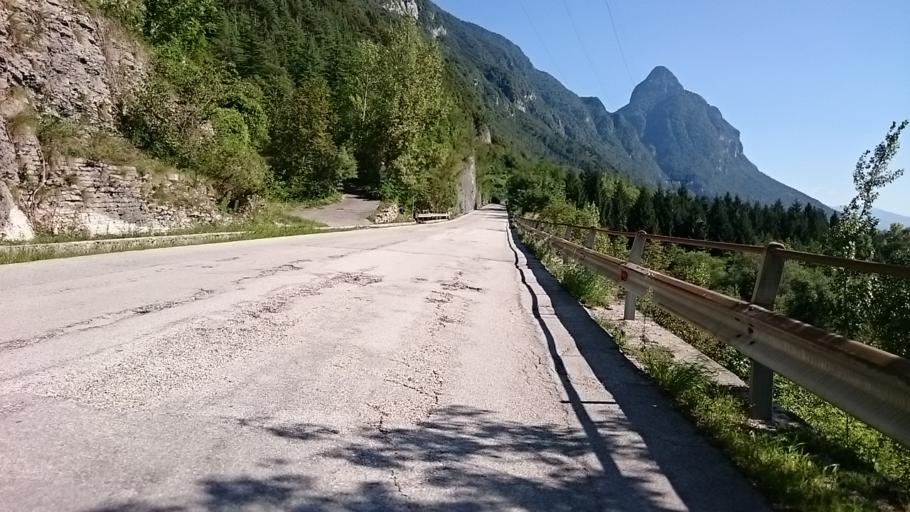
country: IT
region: Veneto
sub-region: Provincia di Belluno
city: Longarone
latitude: 46.2671
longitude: 12.3115
